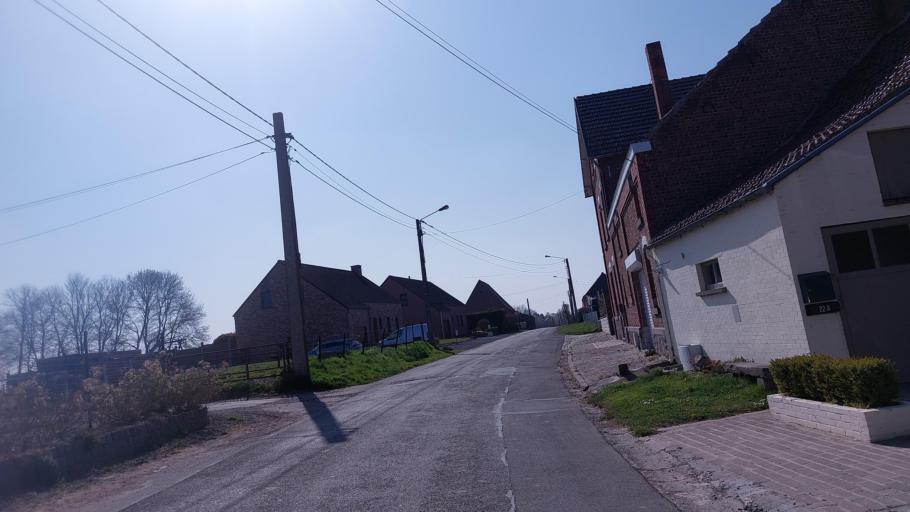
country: BE
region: Wallonia
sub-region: Province du Hainaut
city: Soignies
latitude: 50.5267
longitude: 4.0396
